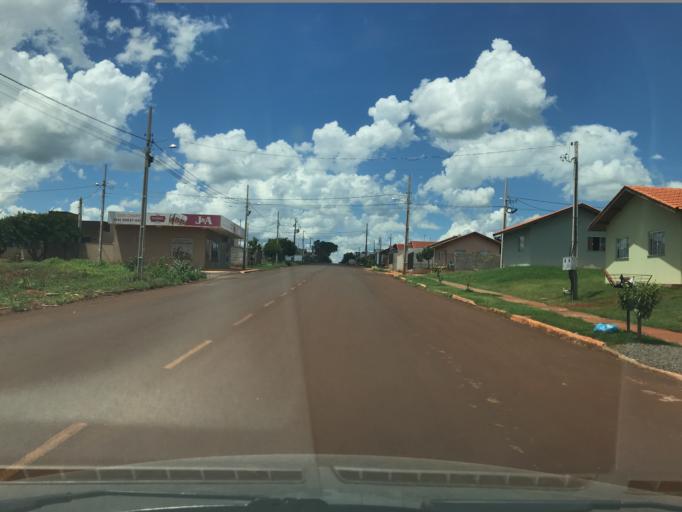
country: BR
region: Parana
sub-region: Palotina
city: Palotina
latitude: -24.2649
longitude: -53.8469
